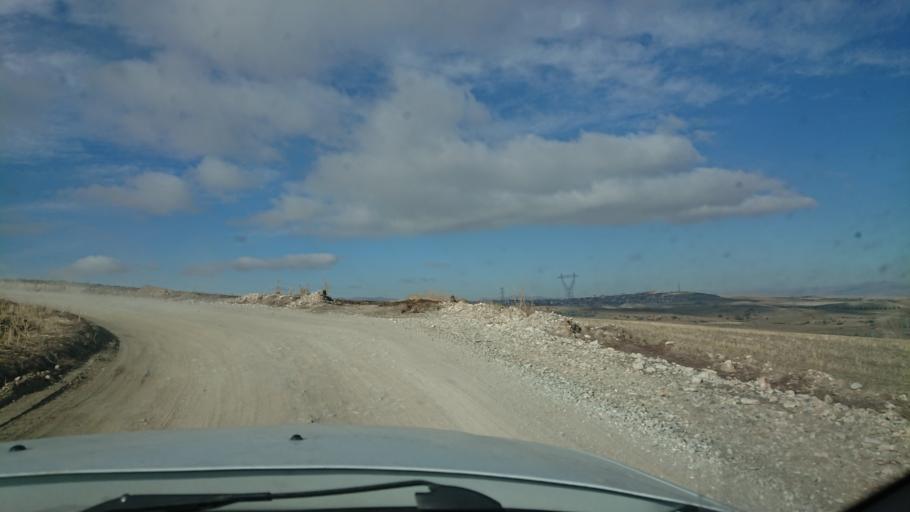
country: TR
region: Aksaray
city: Agacoren
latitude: 38.8494
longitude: 33.9471
